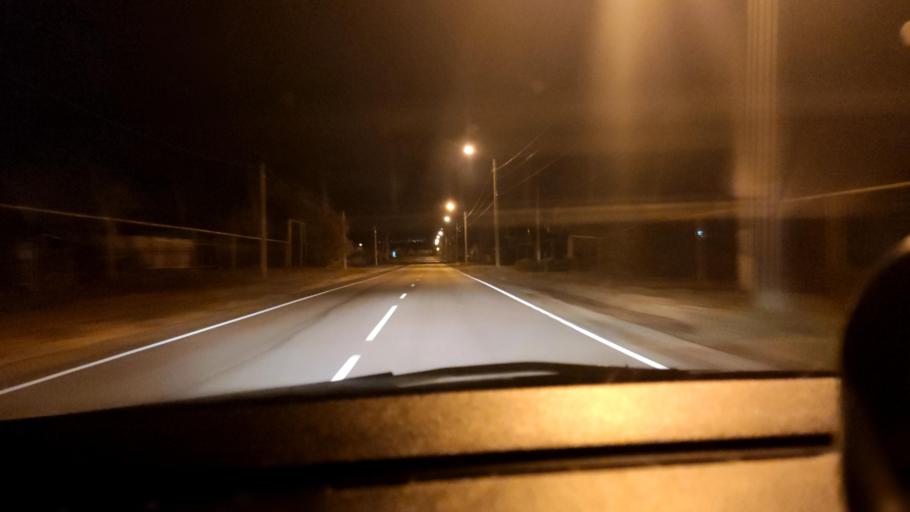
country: RU
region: Voronezj
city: Shilovo
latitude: 51.5535
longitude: 39.0681
